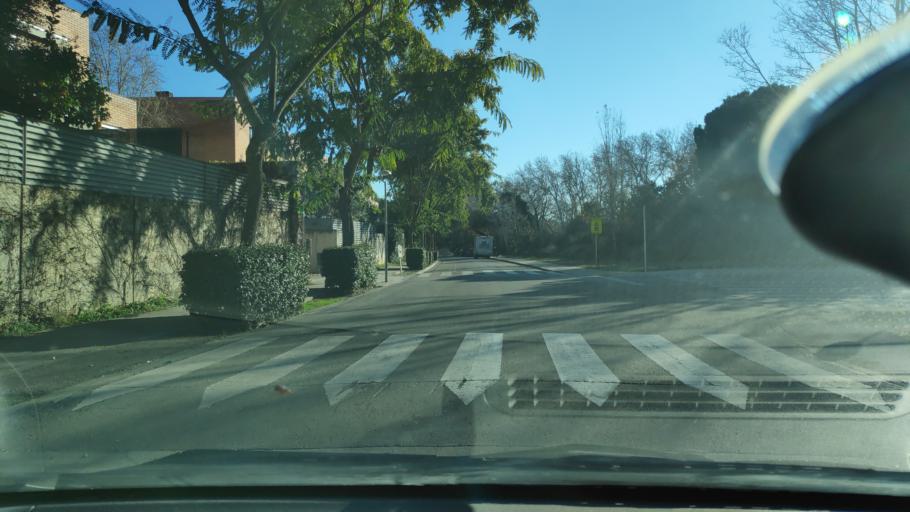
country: ES
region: Catalonia
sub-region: Provincia de Barcelona
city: Sant Quirze del Valles
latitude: 41.5416
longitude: 2.0682
